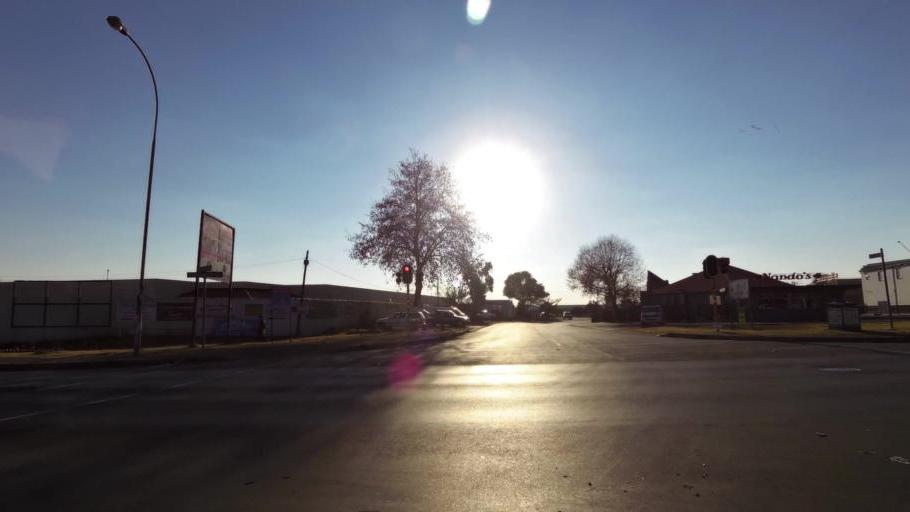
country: ZA
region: Gauteng
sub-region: City of Johannesburg Metropolitan Municipality
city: Johannesburg
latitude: -26.2425
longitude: 28.0050
